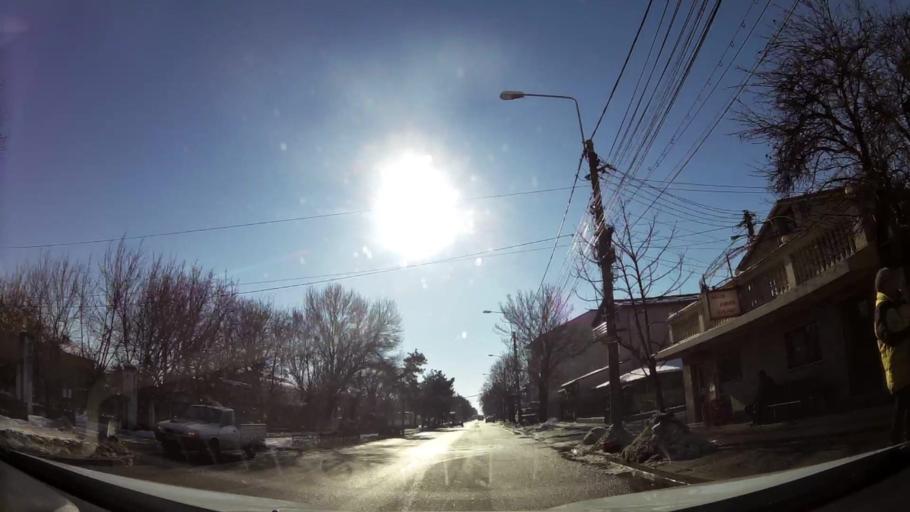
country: RO
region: Ilfov
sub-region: Comuna Magurele
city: Magurele
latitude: 44.3931
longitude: 26.0480
